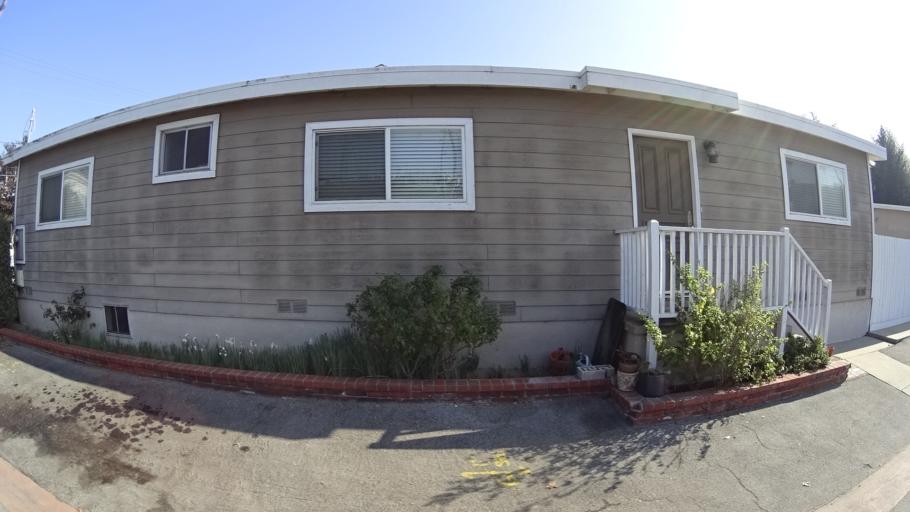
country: US
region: California
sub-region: Los Angeles County
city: Manhattan Beach
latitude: 33.8952
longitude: -118.4097
